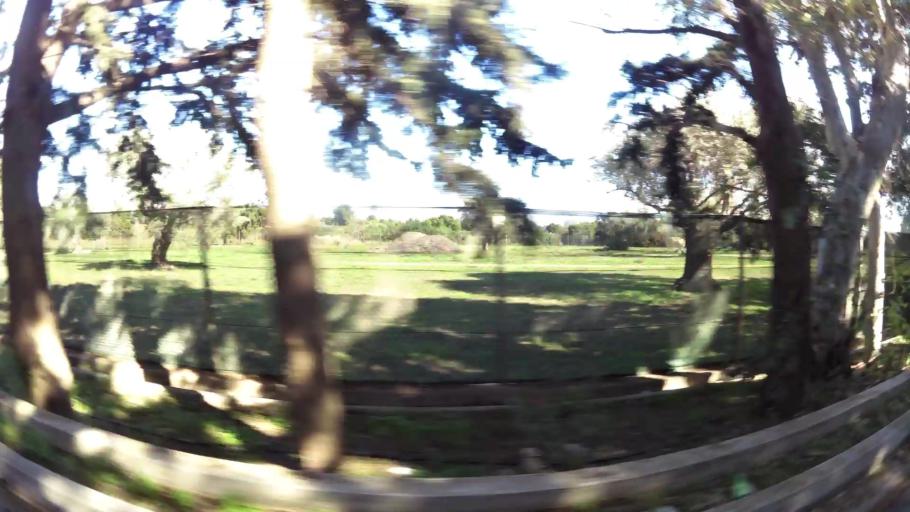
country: GR
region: Attica
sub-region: Nomarchia Anatolikis Attikis
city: Pikermi
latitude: 38.0093
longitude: 23.9369
